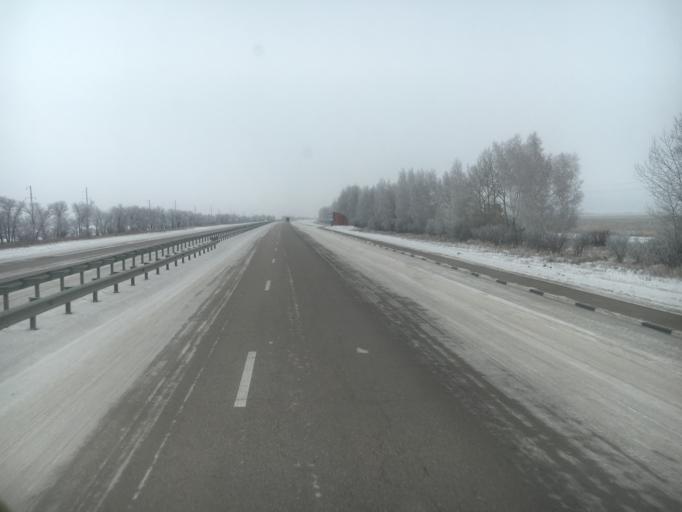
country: KZ
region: Aqmola
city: Akkol'
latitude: 53.3393
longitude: 69.5017
